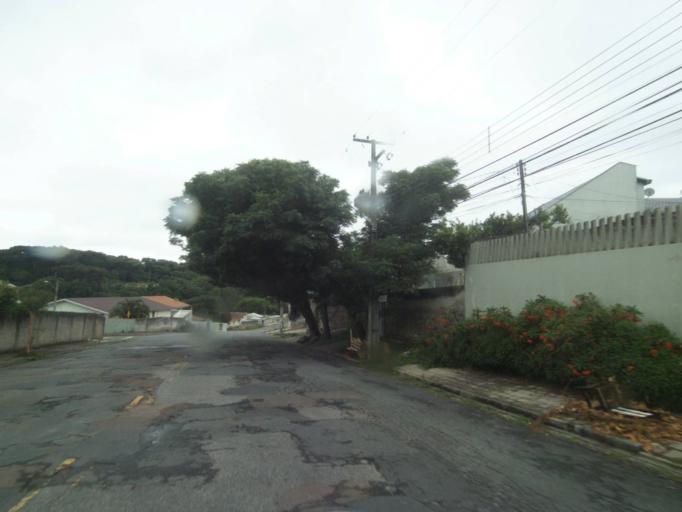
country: BR
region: Parana
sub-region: Curitiba
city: Curitiba
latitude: -25.4294
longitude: -49.3456
